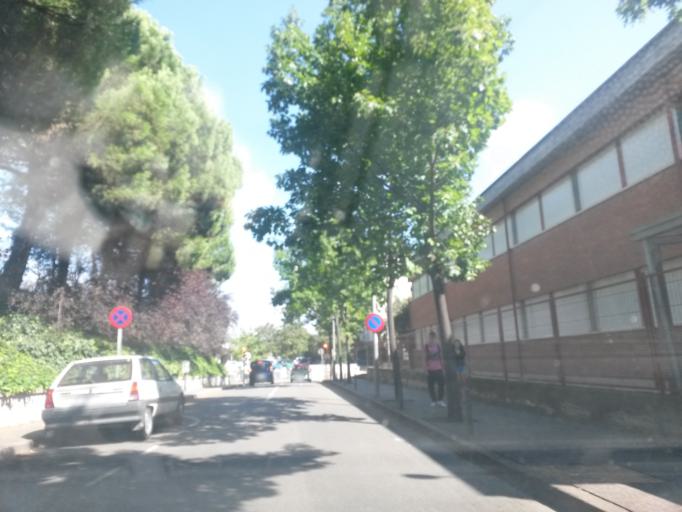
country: ES
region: Catalonia
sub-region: Provincia de Girona
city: Girona
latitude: 41.9733
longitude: 2.8147
